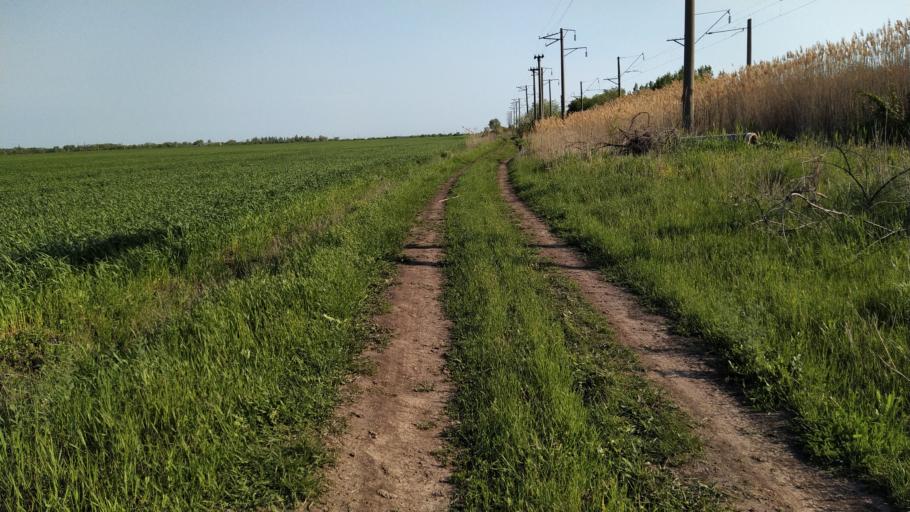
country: RU
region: Rostov
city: Bataysk
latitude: 47.1160
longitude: 39.7138
